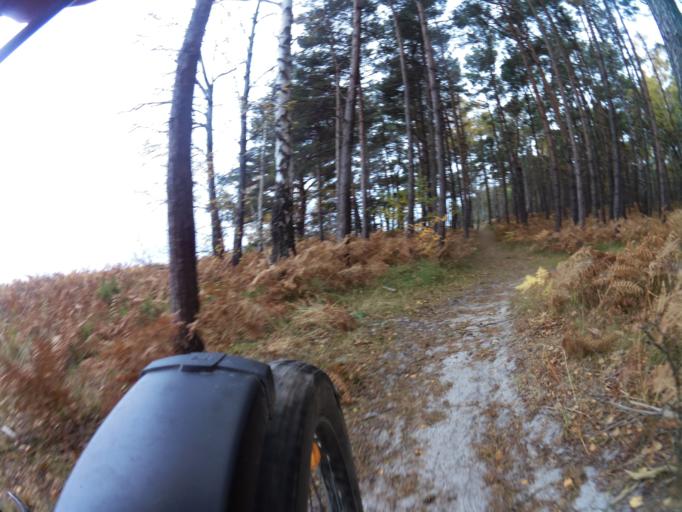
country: PL
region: Pomeranian Voivodeship
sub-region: Powiat pucki
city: Jastarnia
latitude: 54.6869
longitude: 18.7037
